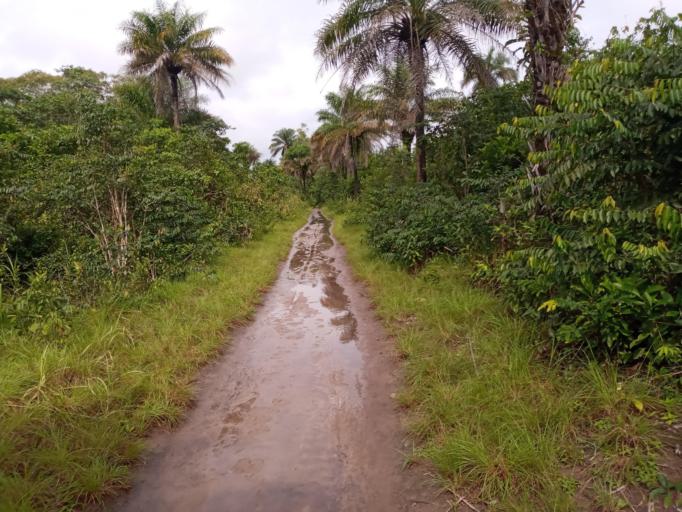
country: SL
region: Southern Province
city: Bonthe
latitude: 7.5168
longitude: -12.5432
